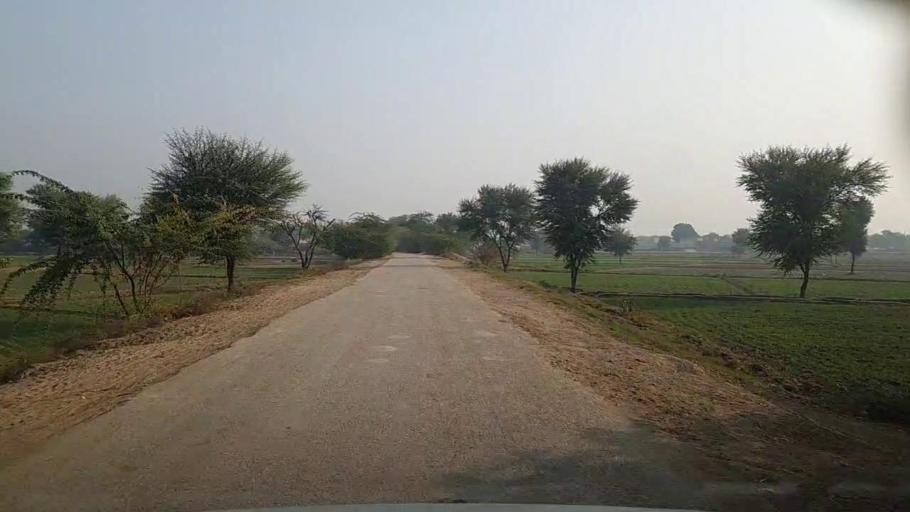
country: PK
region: Sindh
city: Kandiari
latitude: 27.0379
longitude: 68.4801
